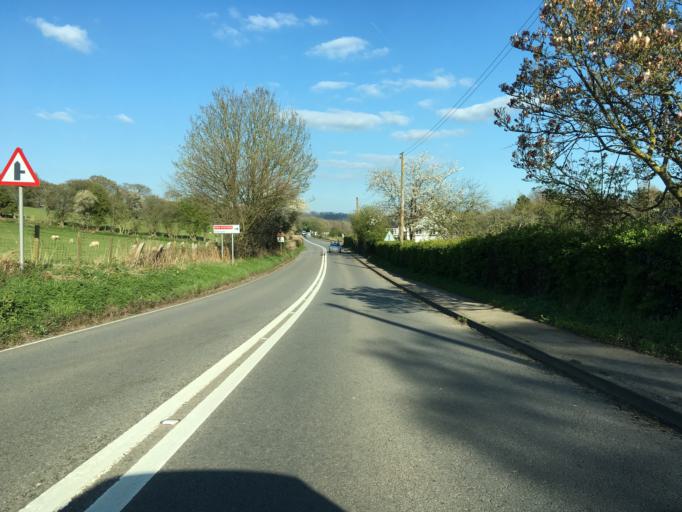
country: GB
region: Wales
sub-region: Monmouthshire
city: Usk
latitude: 51.7185
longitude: -2.9535
